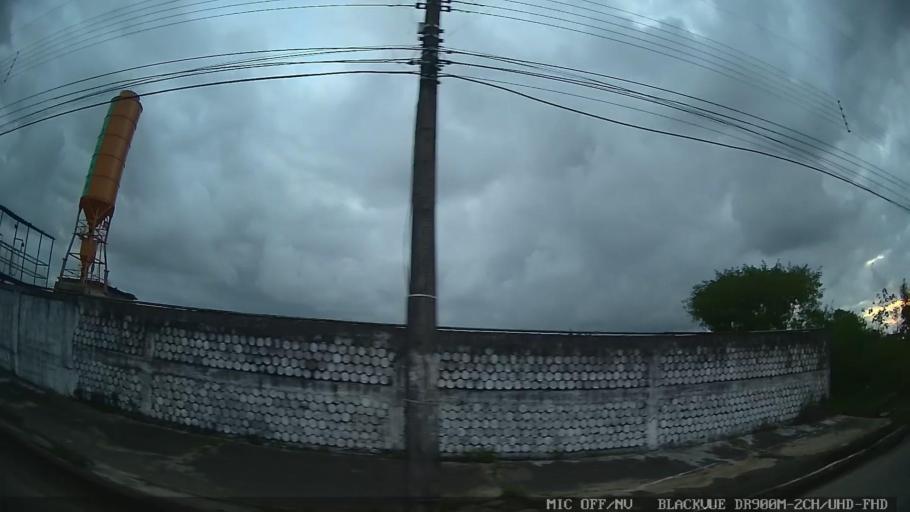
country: BR
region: Sao Paulo
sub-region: Itanhaem
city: Itanhaem
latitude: -24.1871
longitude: -46.8289
